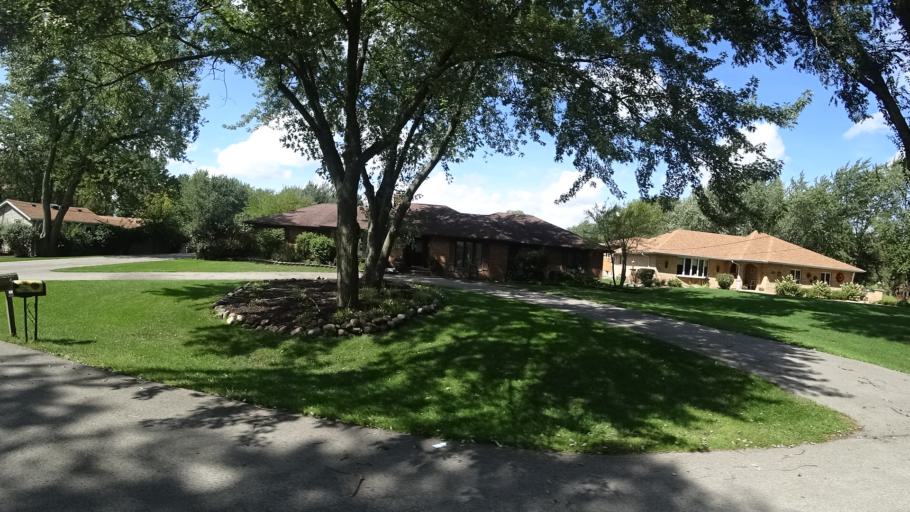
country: US
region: Illinois
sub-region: Cook County
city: Tinley Park
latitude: 41.5646
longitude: -87.7718
